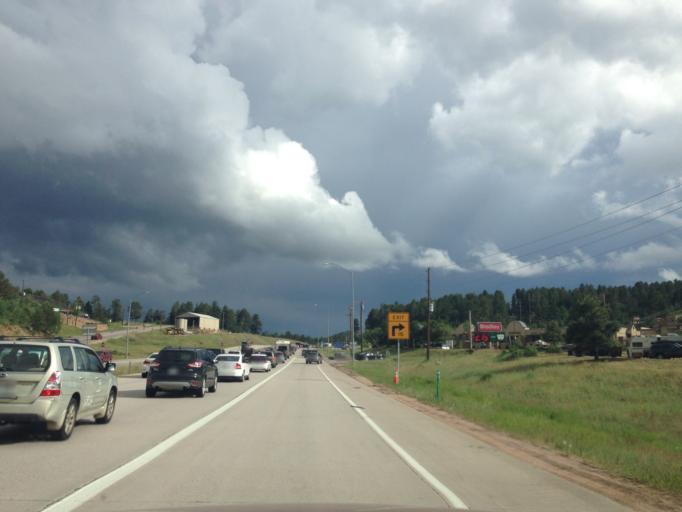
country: US
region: Colorado
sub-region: Jefferson County
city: Evergreen
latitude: 39.5211
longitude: -105.3060
